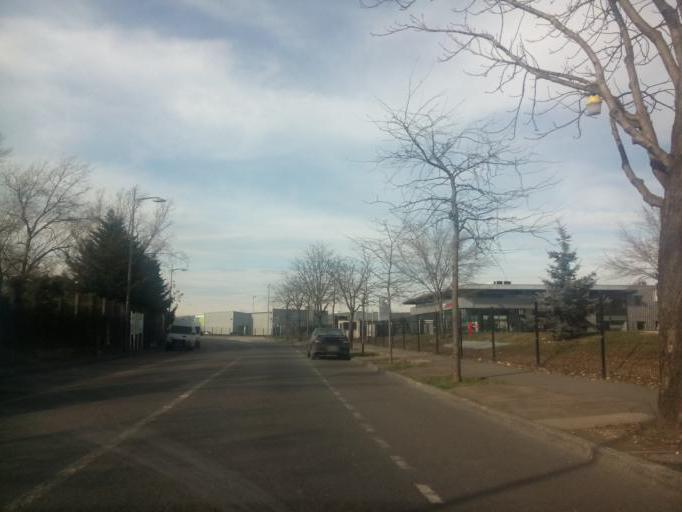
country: FR
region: Rhone-Alpes
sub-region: Departement du Rhone
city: Saint-Fons
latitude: 45.7111
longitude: 4.8462
